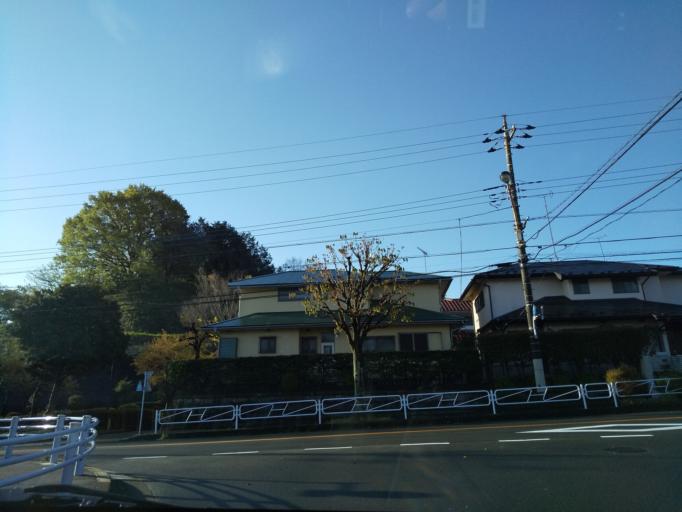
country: JP
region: Tokyo
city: Hachioji
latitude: 35.6241
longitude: 139.3531
